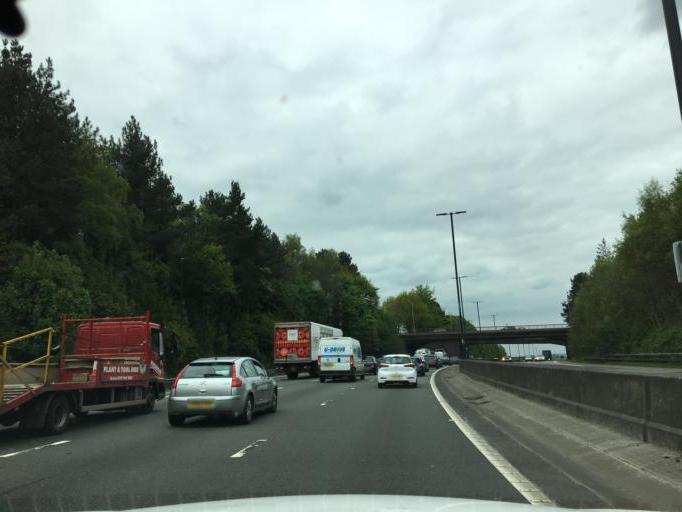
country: GB
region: Wales
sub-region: Newport
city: Newport
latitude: 51.5832
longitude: -3.0359
